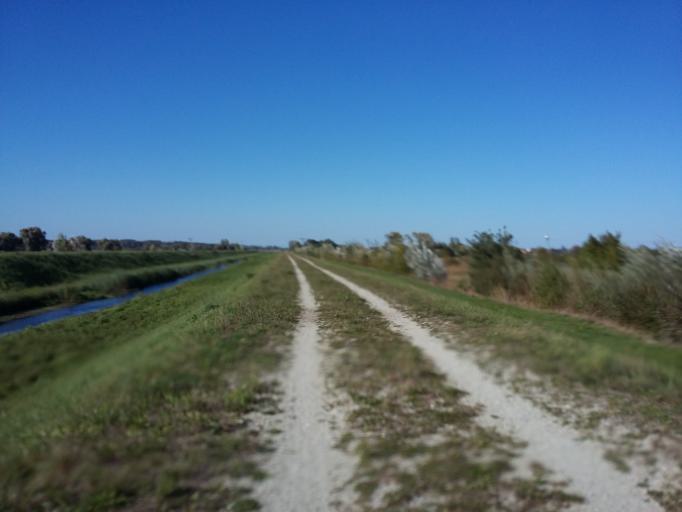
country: SK
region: Bratislavsky
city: Stupava
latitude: 48.3075
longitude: 16.9728
